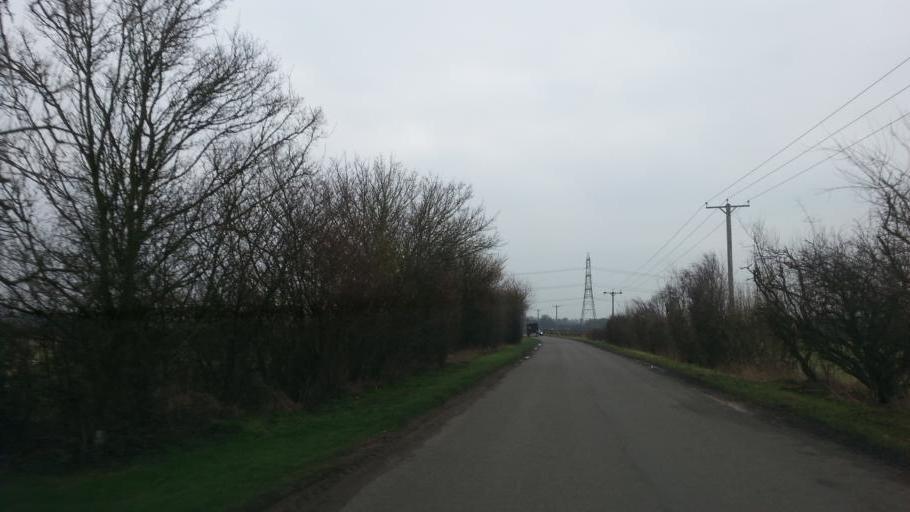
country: GB
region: England
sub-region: Lincolnshire
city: Long Bennington
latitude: 53.0015
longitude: -0.7759
